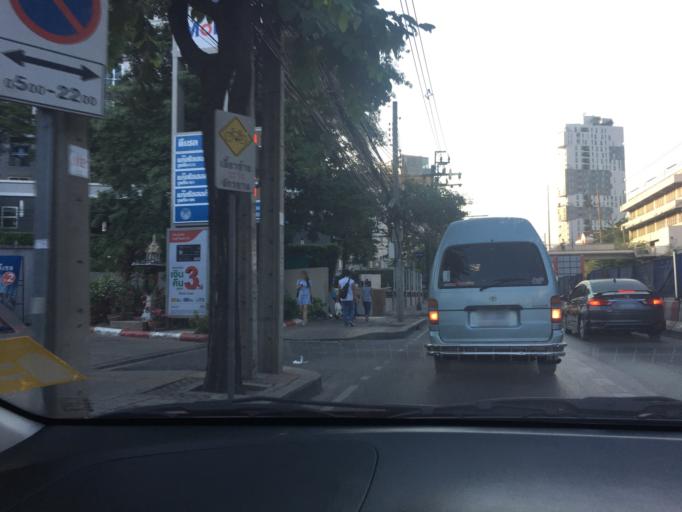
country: TH
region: Bangkok
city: Huai Khwang
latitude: 13.8036
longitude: 100.5781
